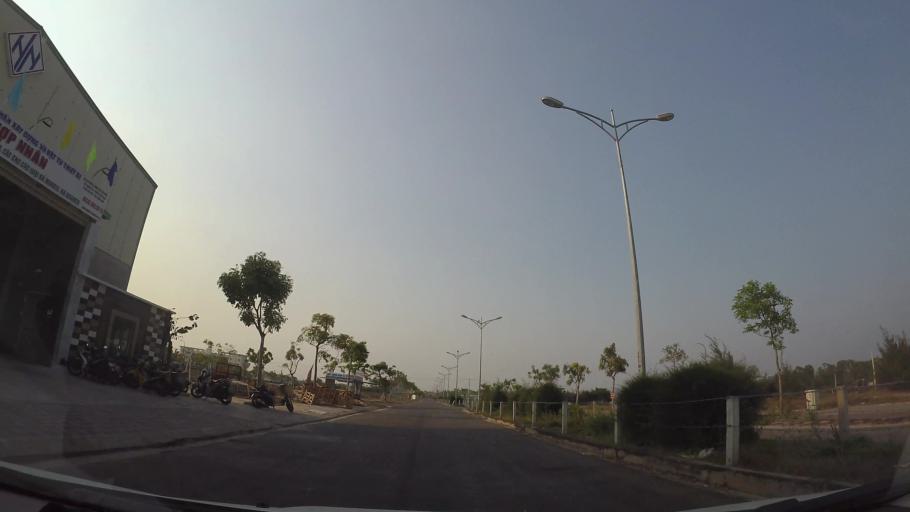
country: VN
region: Da Nang
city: Ngu Hanh Son
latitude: 15.9604
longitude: 108.2615
